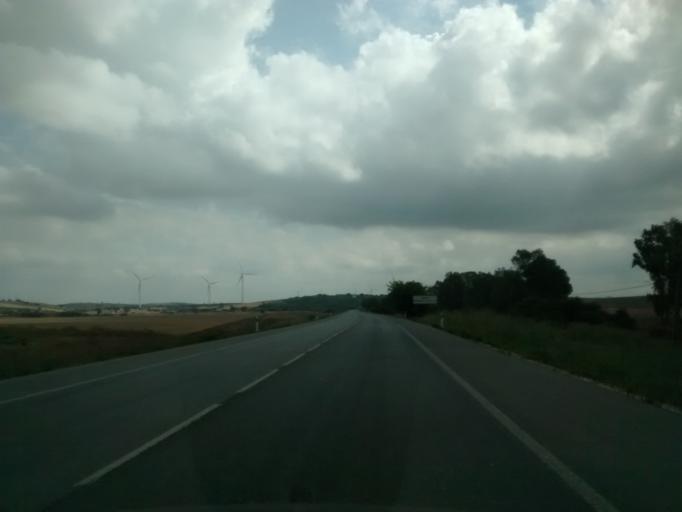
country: ES
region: Andalusia
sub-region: Provincia de Cadiz
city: Chiclana de la Frontera
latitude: 36.4179
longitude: -6.1139
